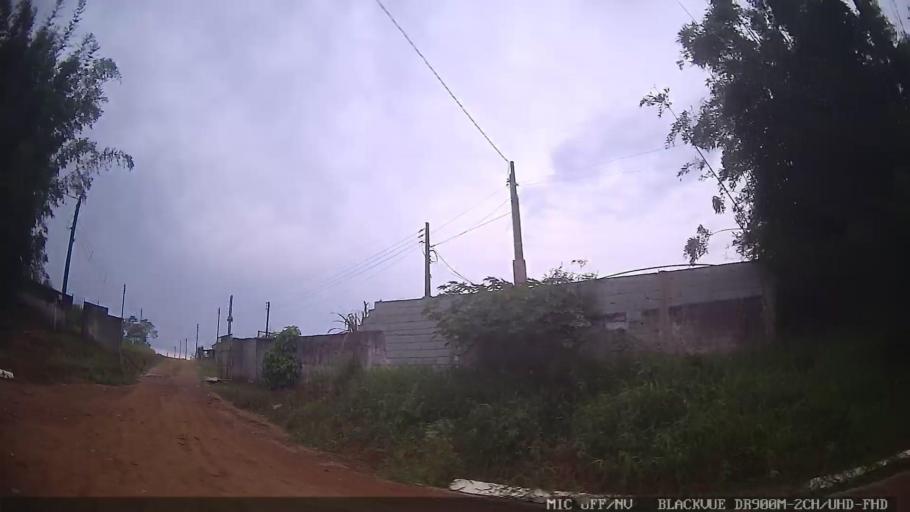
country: BR
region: Sao Paulo
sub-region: Suzano
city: Suzano
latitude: -23.6490
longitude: -46.2704
